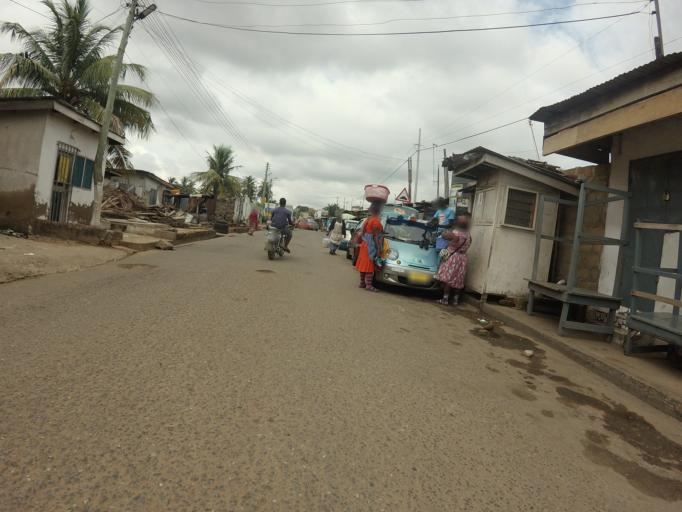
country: GH
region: Greater Accra
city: Accra
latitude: 5.5883
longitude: -0.2004
